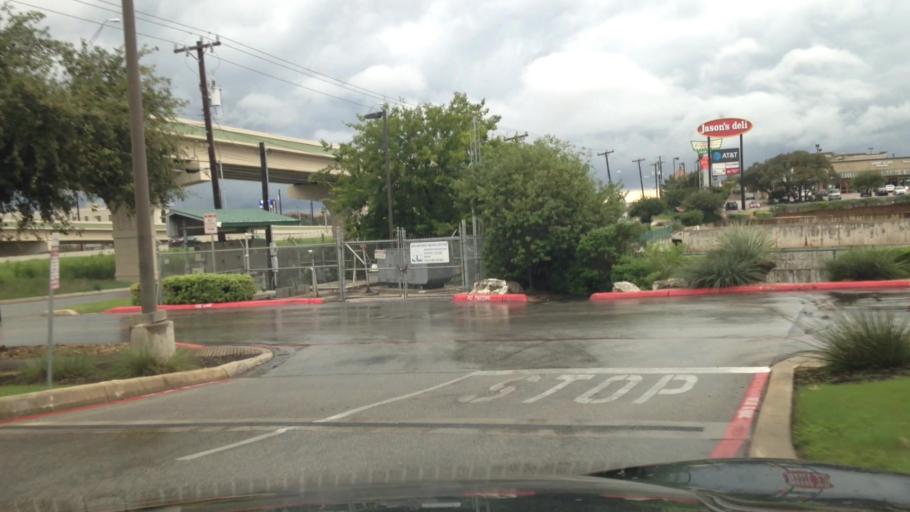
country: US
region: Texas
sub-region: Bexar County
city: Hollywood Park
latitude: 29.6109
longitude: -98.4742
